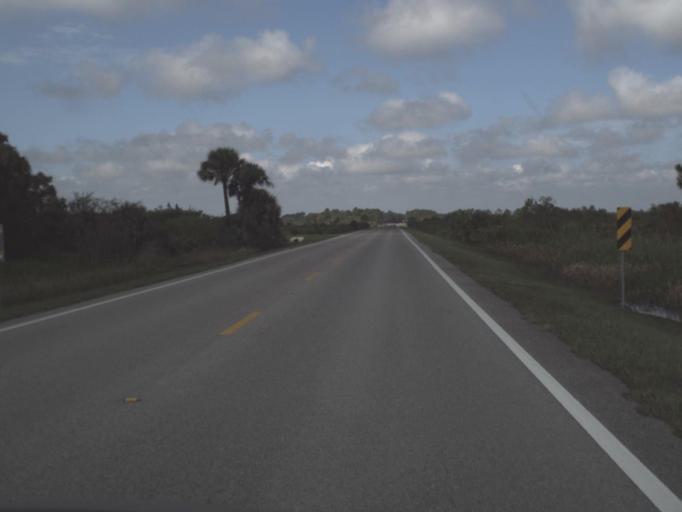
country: US
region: Florida
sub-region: Sarasota County
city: Warm Mineral Springs
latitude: 27.2201
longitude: -82.2861
